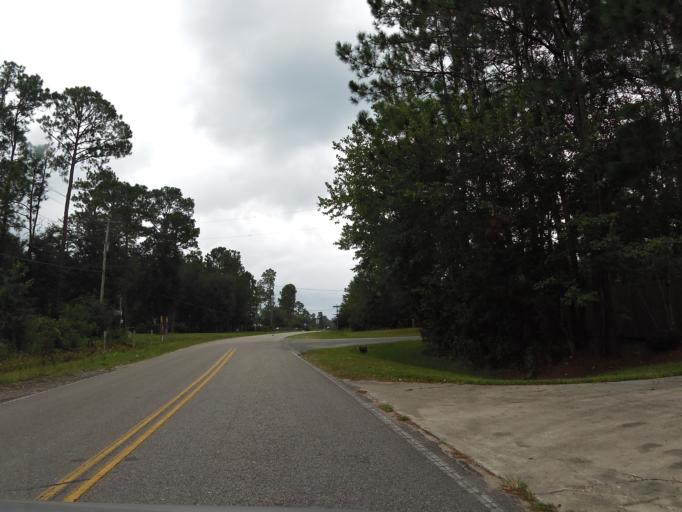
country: US
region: Florida
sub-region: Clay County
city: Middleburg
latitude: 30.1201
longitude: -81.9492
